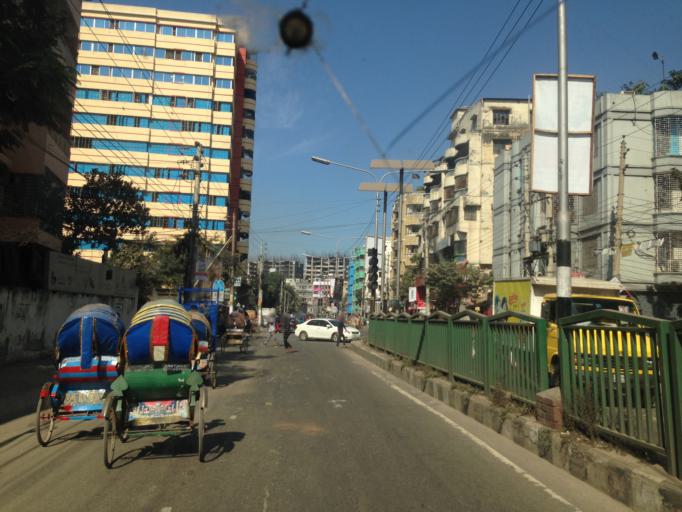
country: BD
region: Dhaka
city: Azimpur
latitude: 23.8091
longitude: 90.3612
